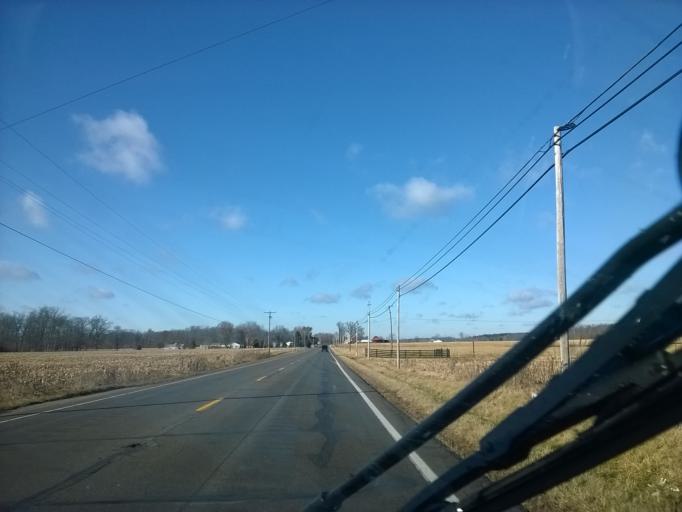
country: US
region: Indiana
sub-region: Jefferson County
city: Hanover
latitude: 38.7129
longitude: -85.4909
